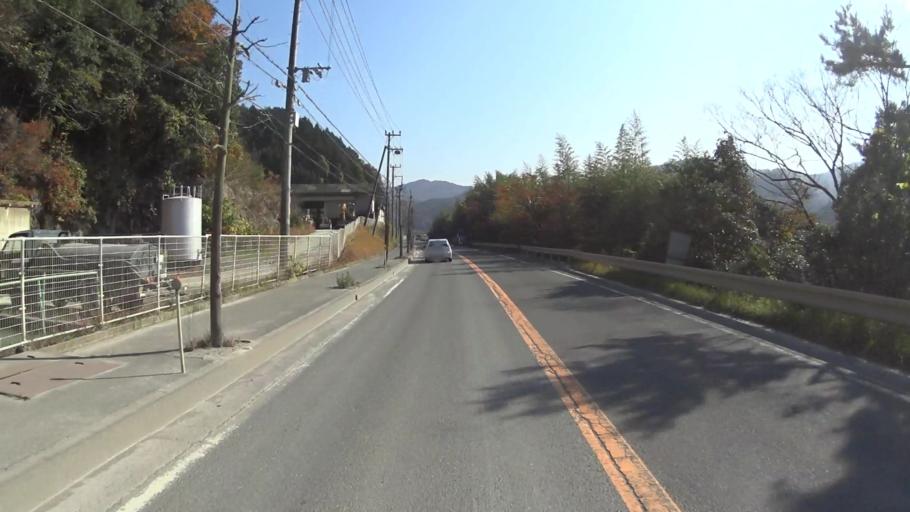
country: JP
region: Kyoto
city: Maizuru
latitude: 35.4283
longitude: 135.2352
